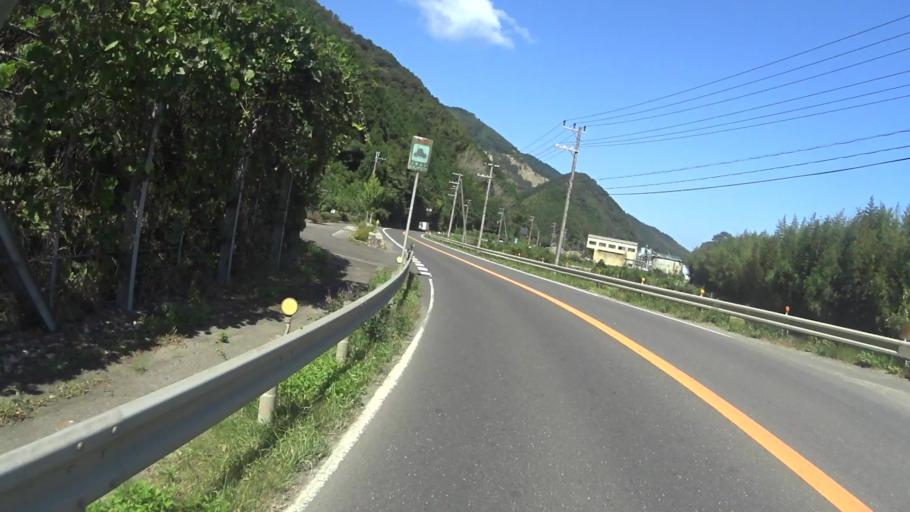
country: JP
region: Kyoto
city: Maizuru
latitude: 35.4785
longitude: 135.2784
